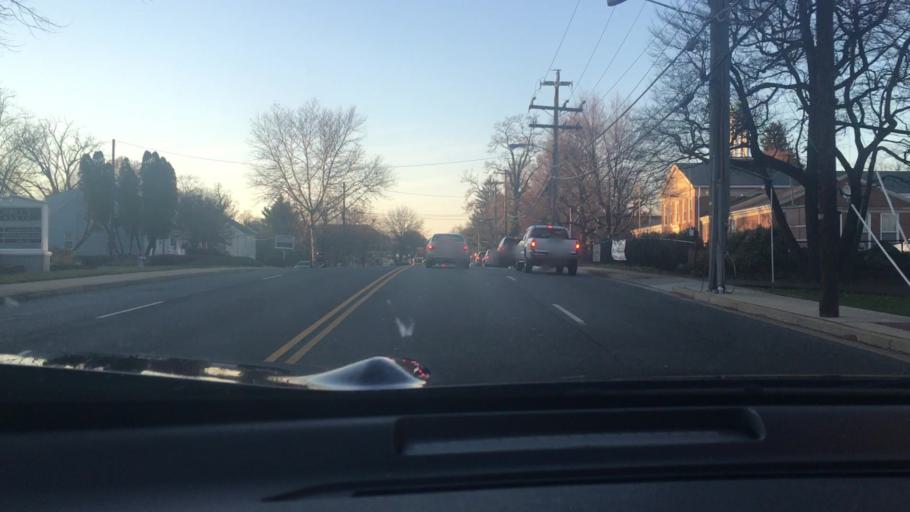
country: US
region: Virginia
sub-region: City of Falls Church
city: Falls Church
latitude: 38.8884
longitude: -77.1806
